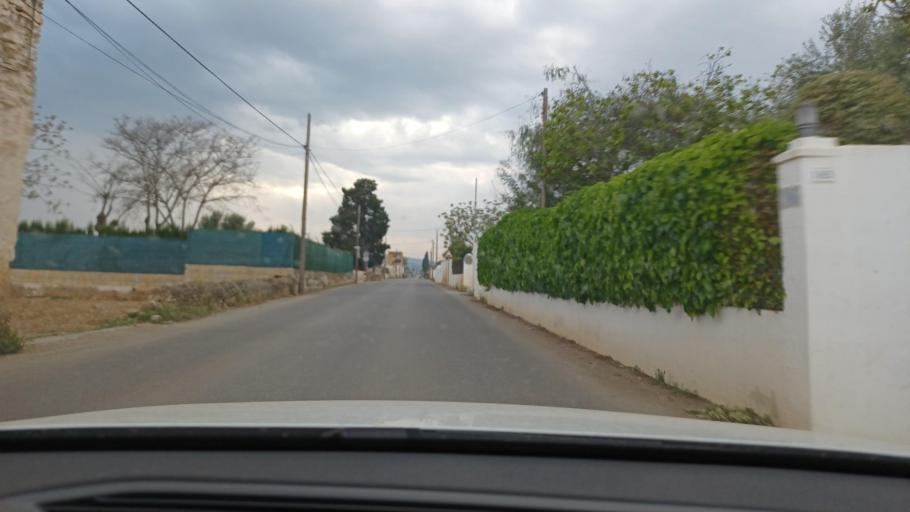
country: ES
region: Valencia
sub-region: Provincia de Castello
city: Benicarlo
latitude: 40.4026
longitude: 0.4104
